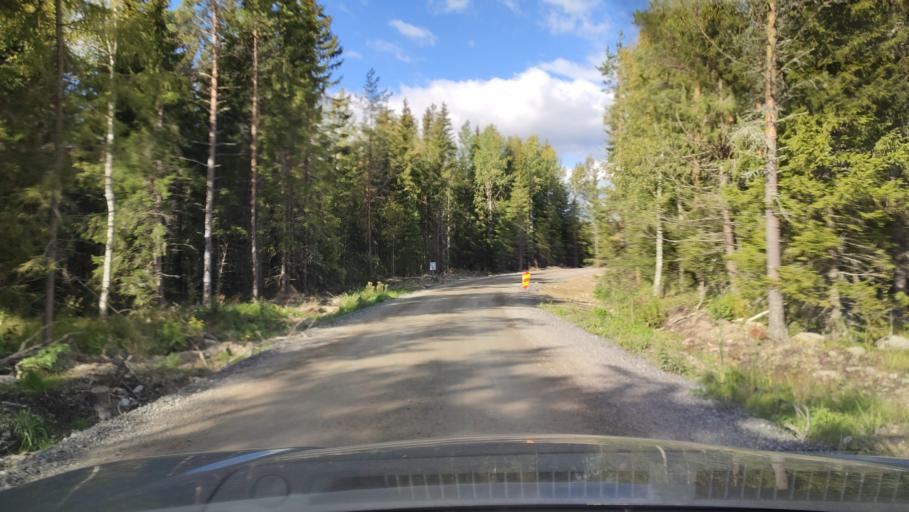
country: FI
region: Southern Ostrobothnia
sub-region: Suupohja
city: Karijoki
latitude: 62.1844
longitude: 21.5893
